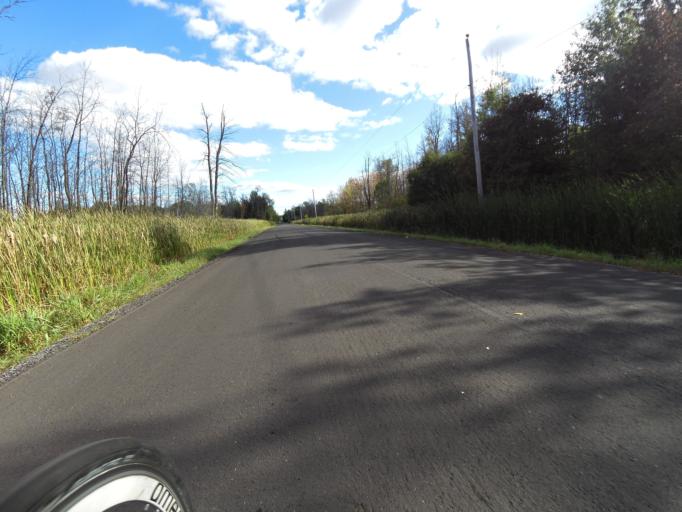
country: CA
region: Ontario
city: Bells Corners
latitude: 45.1031
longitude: -75.6468
